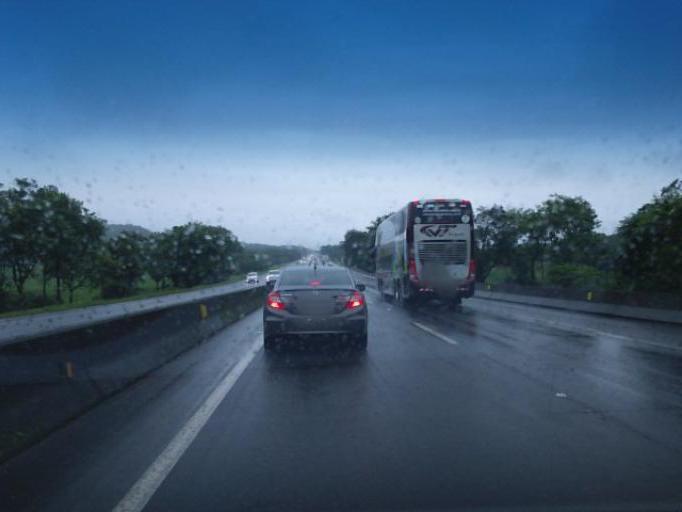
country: BR
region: Santa Catarina
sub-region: Joinville
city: Joinville
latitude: -26.0826
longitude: -48.8618
